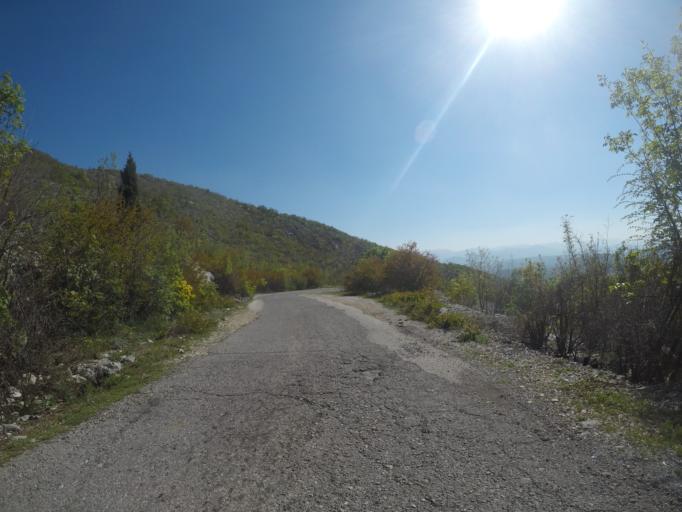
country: ME
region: Danilovgrad
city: Danilovgrad
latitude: 42.5147
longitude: 19.0744
